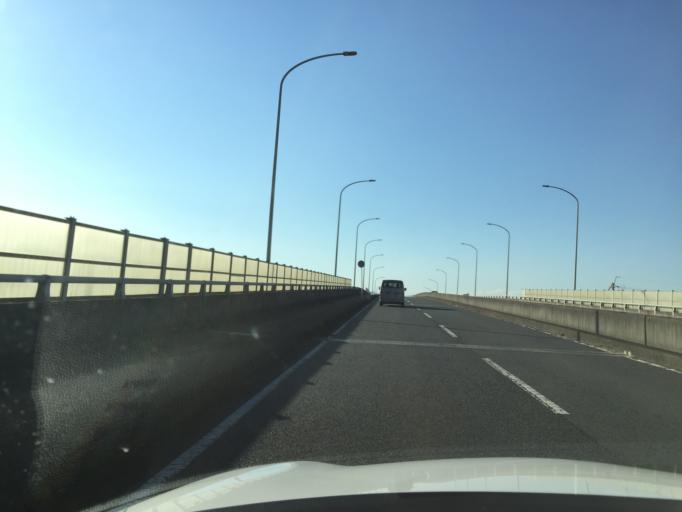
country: JP
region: Fukushima
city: Iwaki
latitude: 36.9864
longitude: 140.8644
